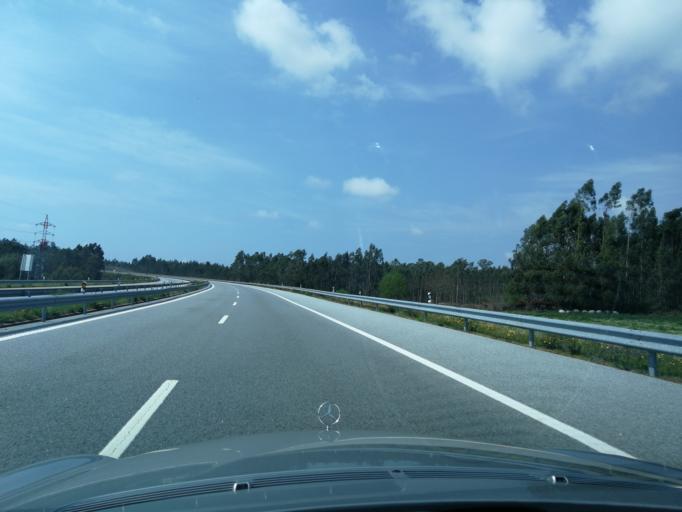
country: PT
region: Braga
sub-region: Vila Nova de Famalicao
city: Ribeirao
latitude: 41.3902
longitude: -8.5882
